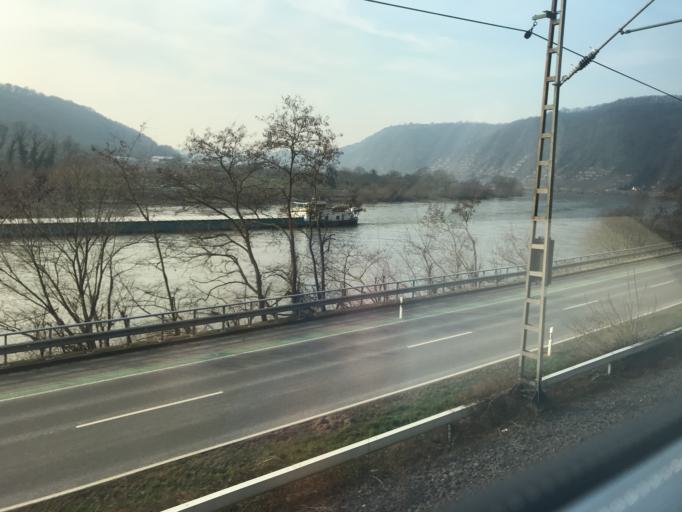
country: DE
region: Rheinland-Pfalz
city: Dieblich
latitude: 50.3187
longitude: 7.4904
